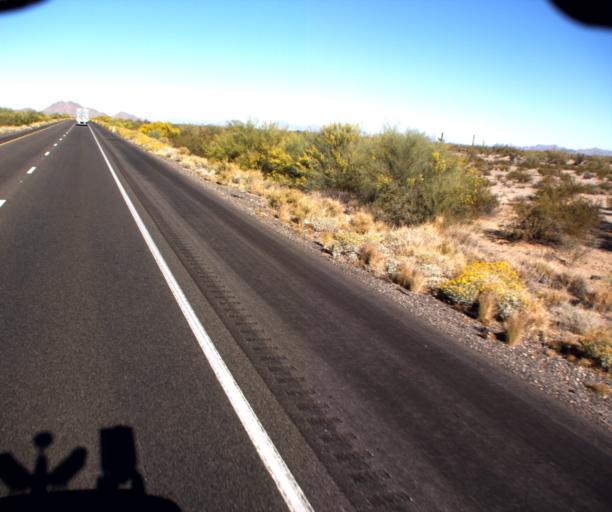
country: US
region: Arizona
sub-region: Maricopa County
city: Gila Bend
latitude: 32.8862
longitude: -112.4701
